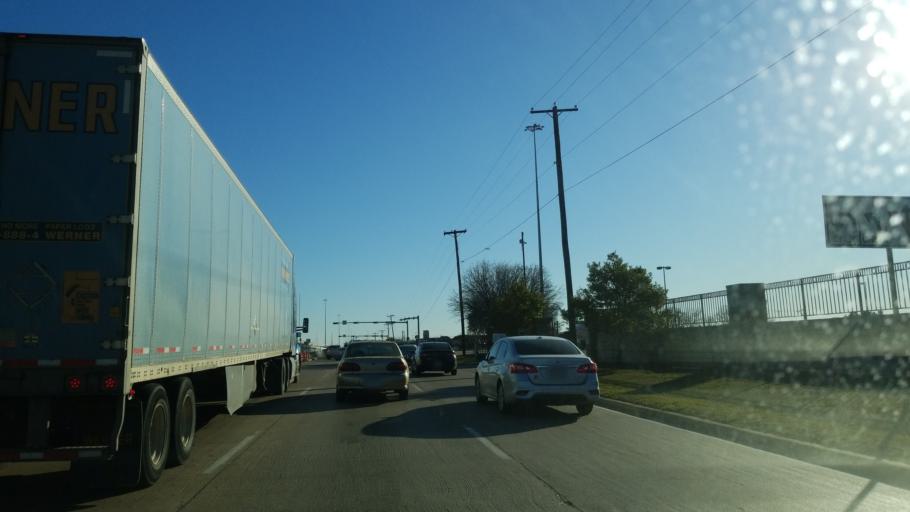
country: US
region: Texas
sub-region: Tarrant County
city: Arlington
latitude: 32.7372
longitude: -97.0631
